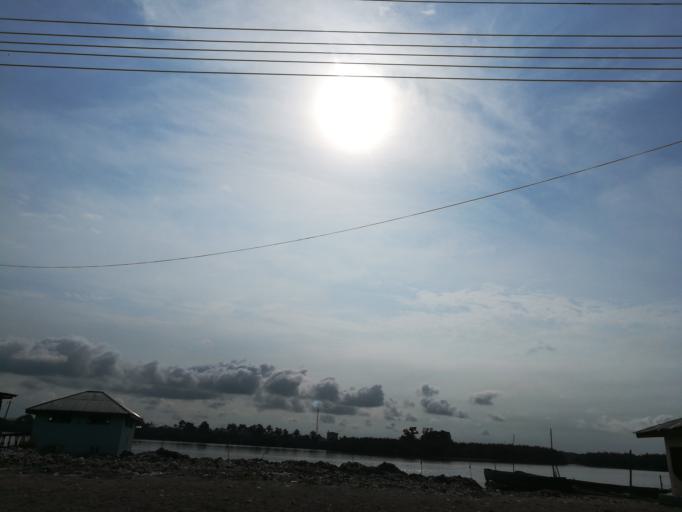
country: NG
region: Rivers
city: Okrika
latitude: 4.7414
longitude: 7.0902
